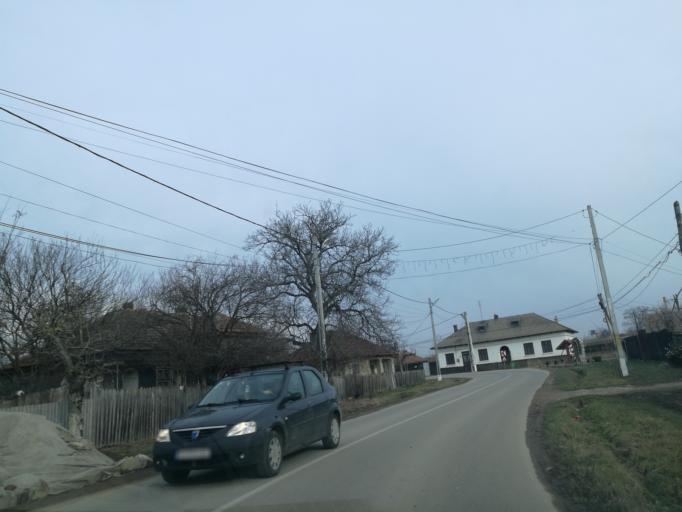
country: RO
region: Ialomita
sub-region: Comuna Fierbinti-Targ
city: Fierbintii de Jos
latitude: 44.6931
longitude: 26.3947
